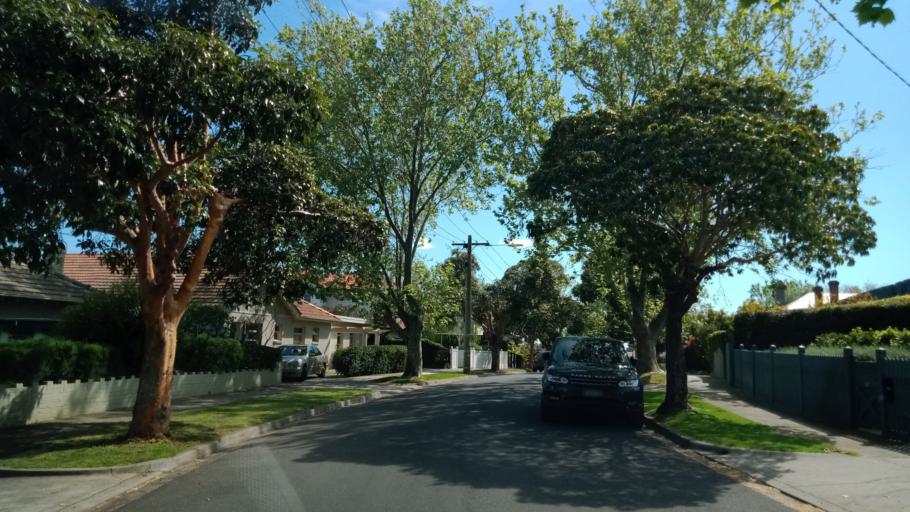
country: AU
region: Victoria
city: Glenferrie
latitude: -37.8369
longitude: 145.0438
